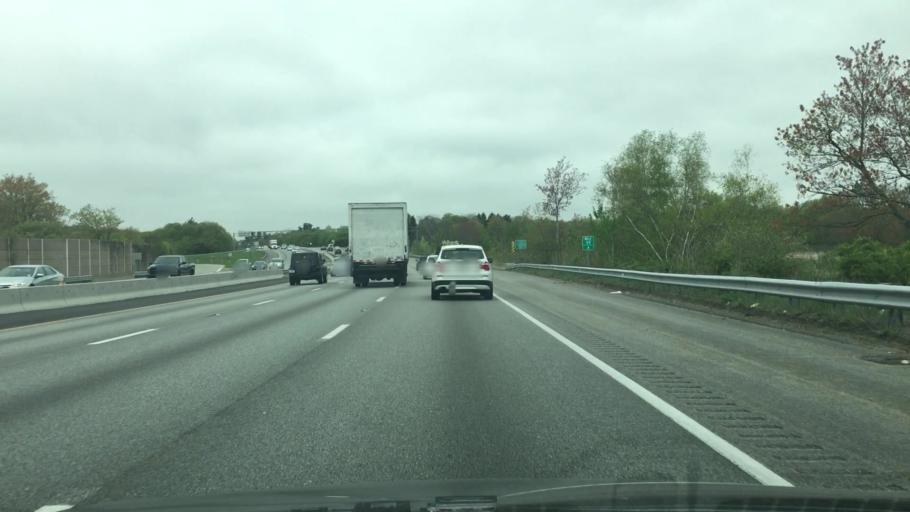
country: US
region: Massachusetts
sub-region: Essex County
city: Lynnfield
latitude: 42.5241
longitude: -71.0608
